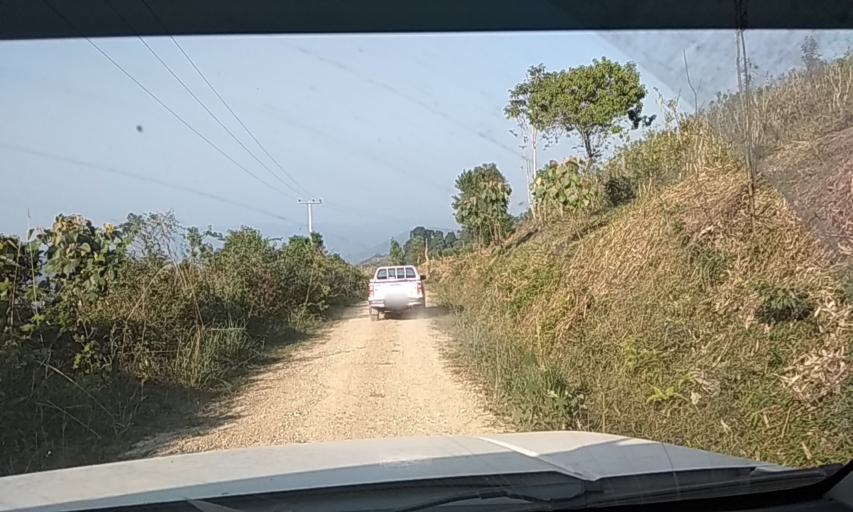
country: LA
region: Phongsali
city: Phongsali
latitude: 21.6611
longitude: 102.1752
